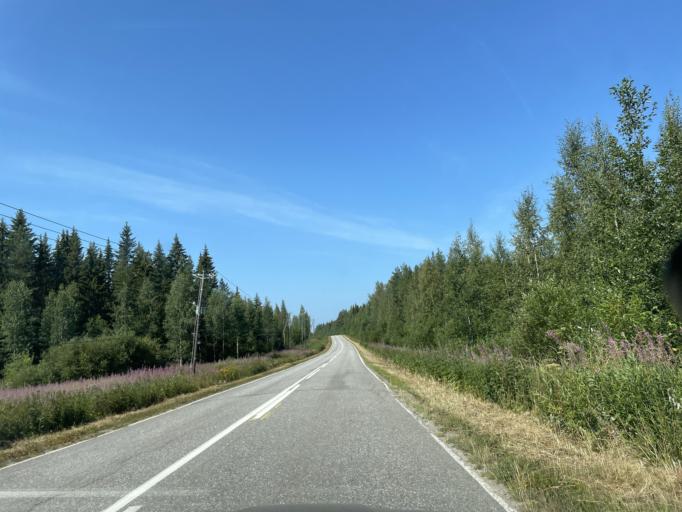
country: FI
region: Central Finland
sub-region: Saarijaervi-Viitasaari
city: Pihtipudas
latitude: 63.3530
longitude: 25.7794
